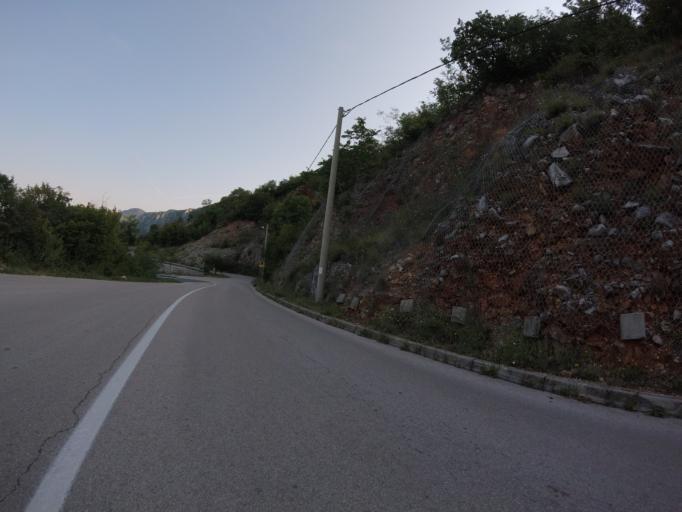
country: HR
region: Primorsko-Goranska
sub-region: Grad Crikvenica
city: Crikvenica
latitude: 45.1955
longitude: 14.7223
